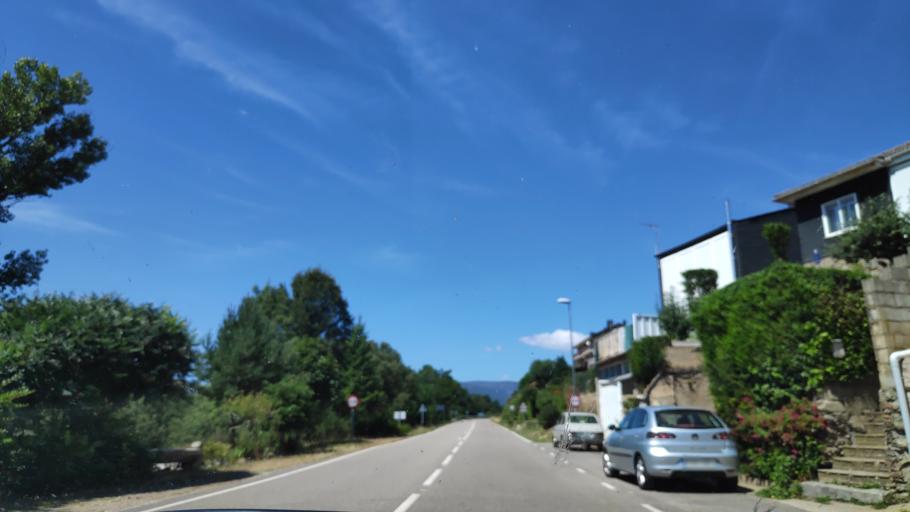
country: ES
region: Castille and Leon
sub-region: Provincia de Zamora
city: Puebla de Sanabria
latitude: 42.0562
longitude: -6.6403
